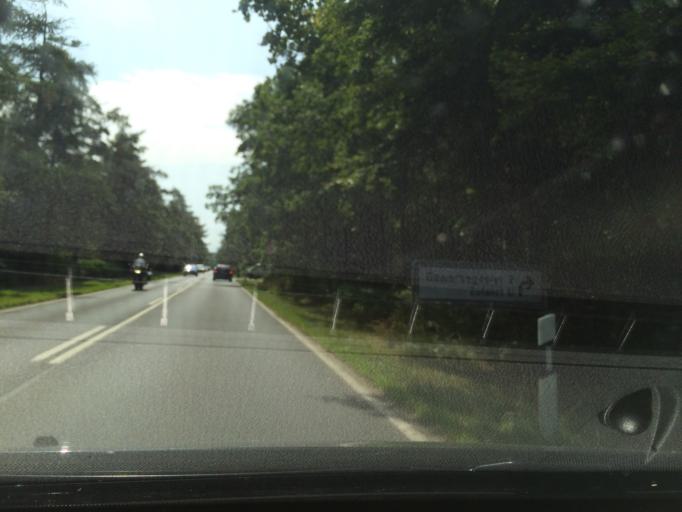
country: DE
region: Mecklenburg-Vorpommern
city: Ostseebad Binz
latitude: 54.4382
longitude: 13.5680
